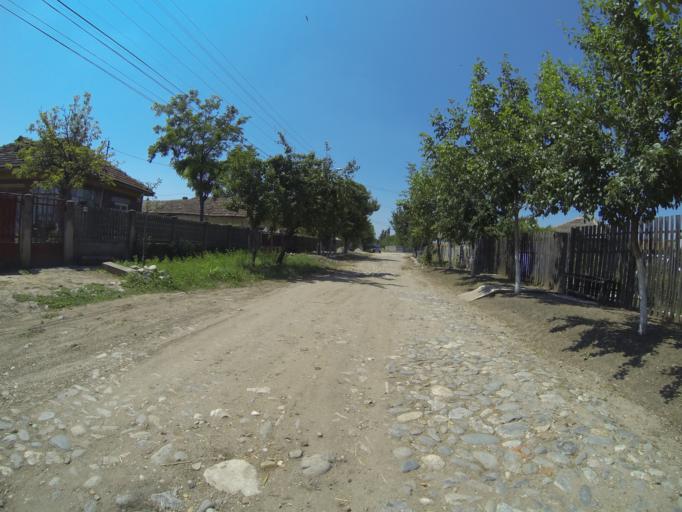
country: RO
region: Dolj
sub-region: Comuna Segarcea
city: Segarcea
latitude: 44.0882
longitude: 23.7403
